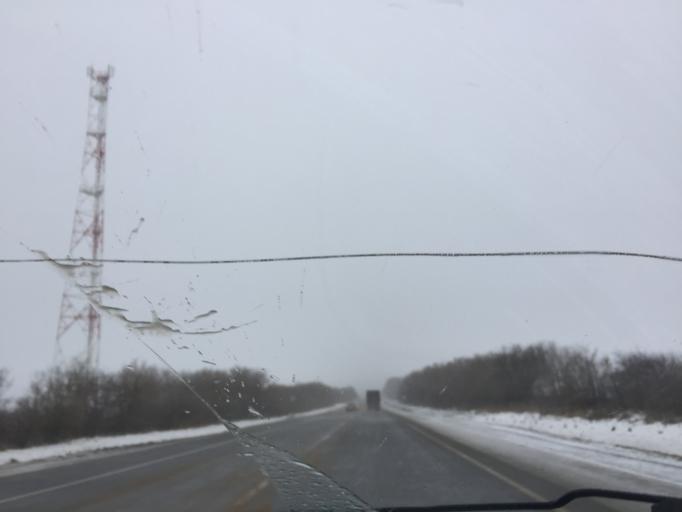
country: RU
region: Tula
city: Plavsk
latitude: 53.7850
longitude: 37.3634
